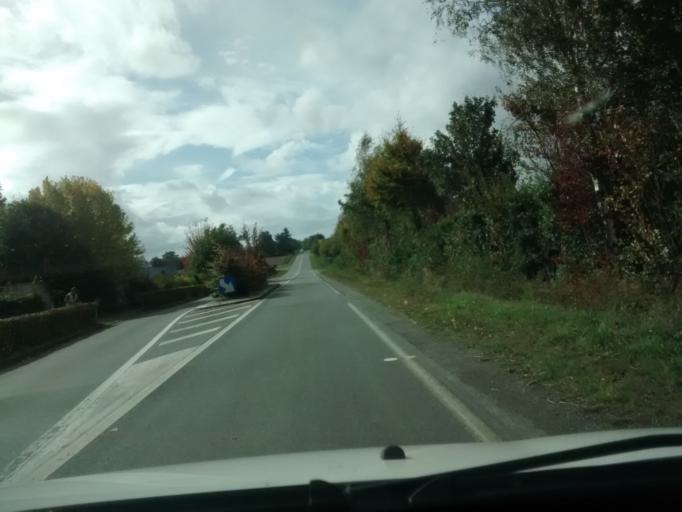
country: FR
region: Brittany
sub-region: Departement d'Ille-et-Vilaine
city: Saint-Didier
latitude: 48.1408
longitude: -1.3469
